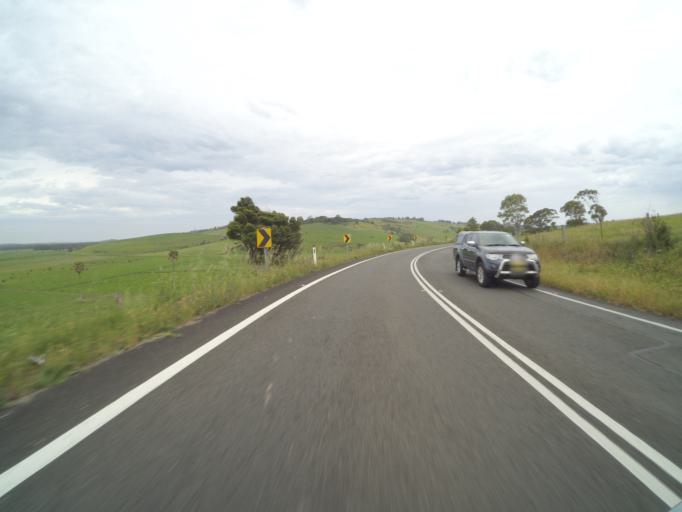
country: AU
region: New South Wales
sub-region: Kiama
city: Kiama
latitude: -34.6540
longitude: 150.8157
